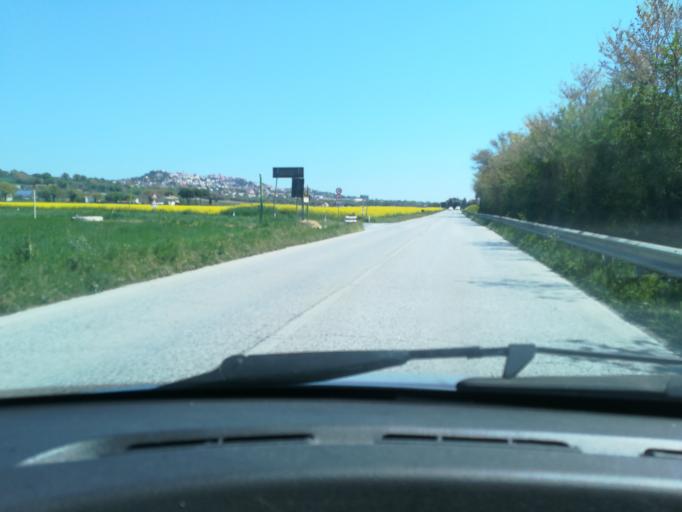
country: IT
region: The Marches
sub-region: Provincia di Ancona
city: Campocavallo
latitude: 43.4574
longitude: 13.5115
